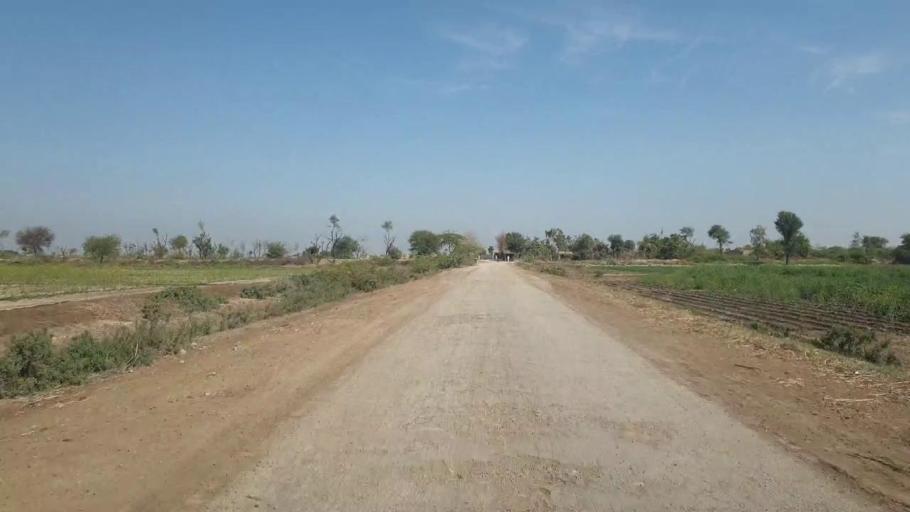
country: PK
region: Sindh
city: Samaro
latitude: 25.3380
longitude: 69.2481
